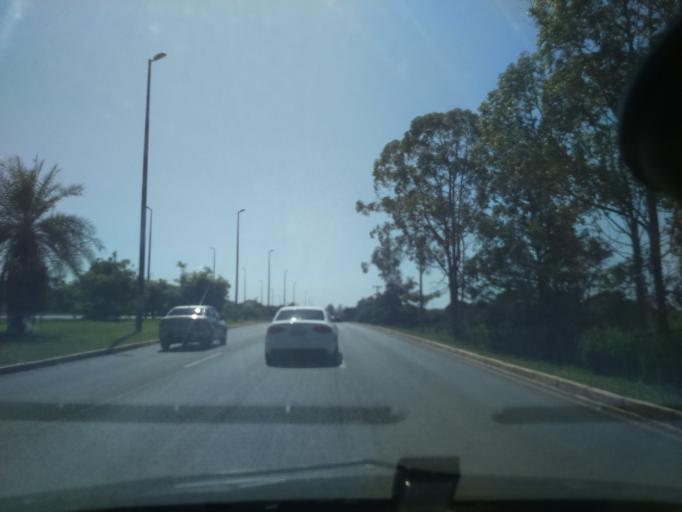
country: BR
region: Federal District
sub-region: Brasilia
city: Brasilia
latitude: -15.8422
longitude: -47.9141
